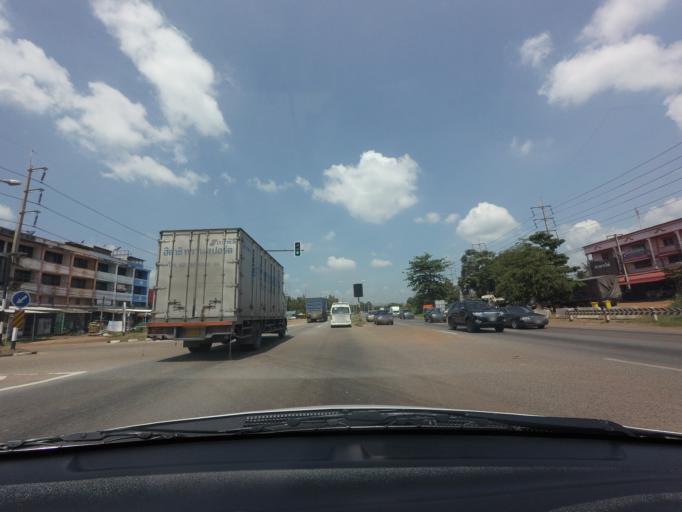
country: TH
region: Prachin Buri
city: Si Maha Phot
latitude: 13.8617
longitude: 101.5548
